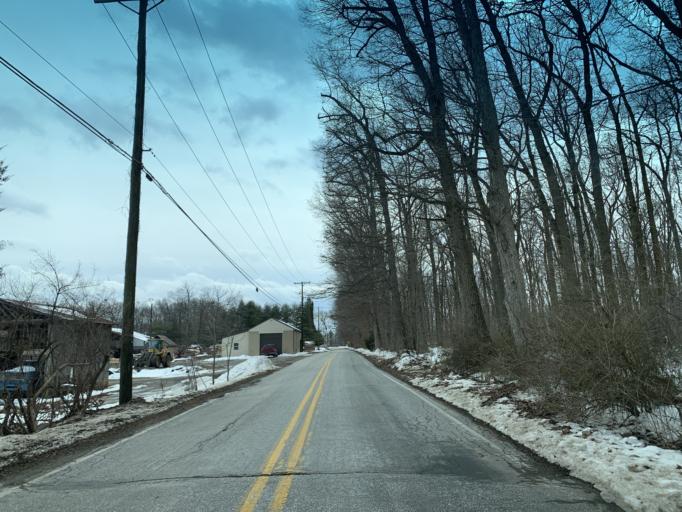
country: US
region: Pennsylvania
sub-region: York County
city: Shrewsbury
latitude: 39.7797
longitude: -76.6332
